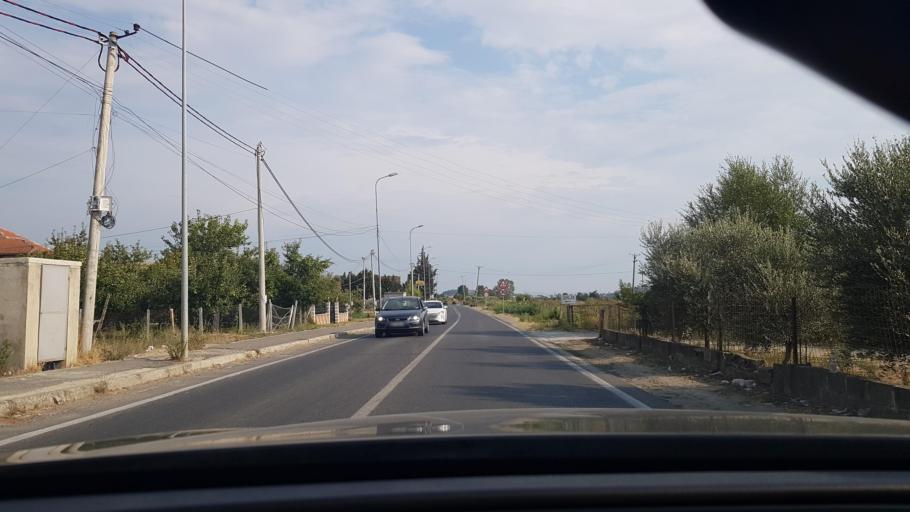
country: AL
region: Durres
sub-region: Rrethi i Durresit
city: Manze
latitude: 41.4626
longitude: 19.5636
